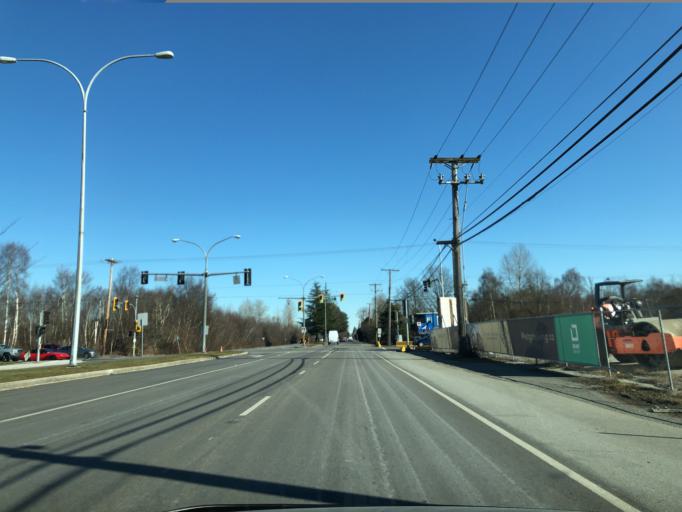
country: CA
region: British Columbia
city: Richmond
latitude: 49.1701
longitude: -123.1154
